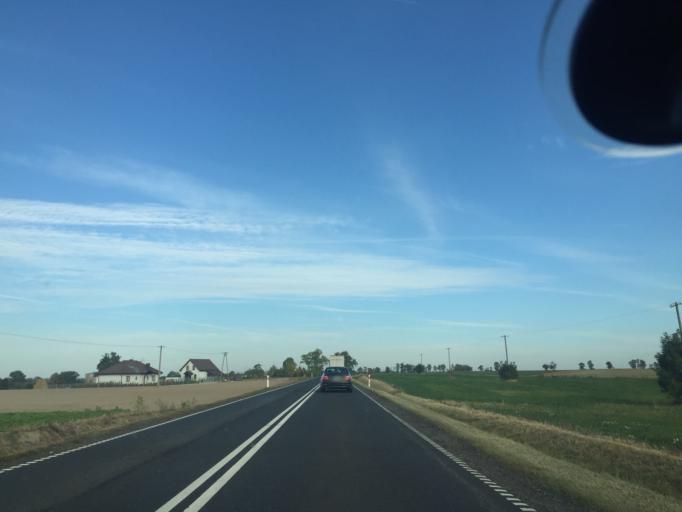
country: PL
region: Kujawsko-Pomorskie
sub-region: Powiat mogilenski
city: Mogilno
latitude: 52.6172
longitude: 17.9597
